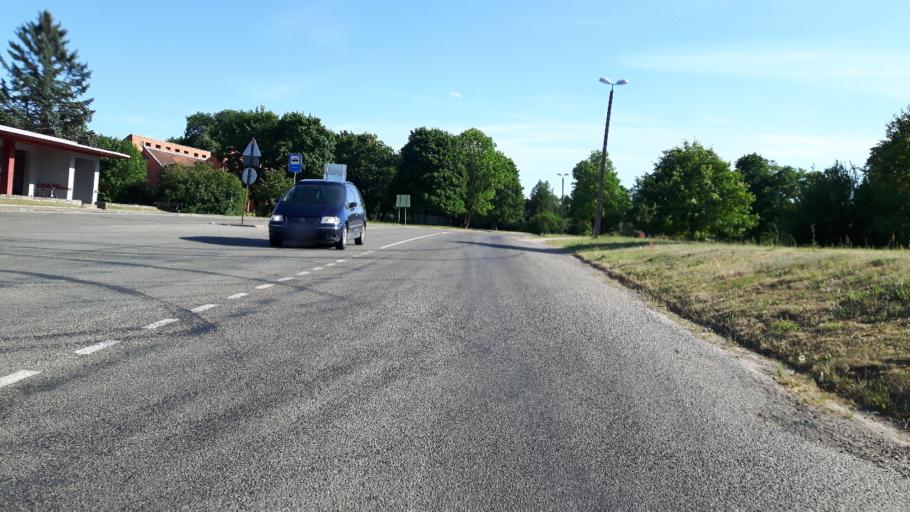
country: LV
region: Talsu Rajons
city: Stende
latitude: 57.0684
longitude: 22.2935
